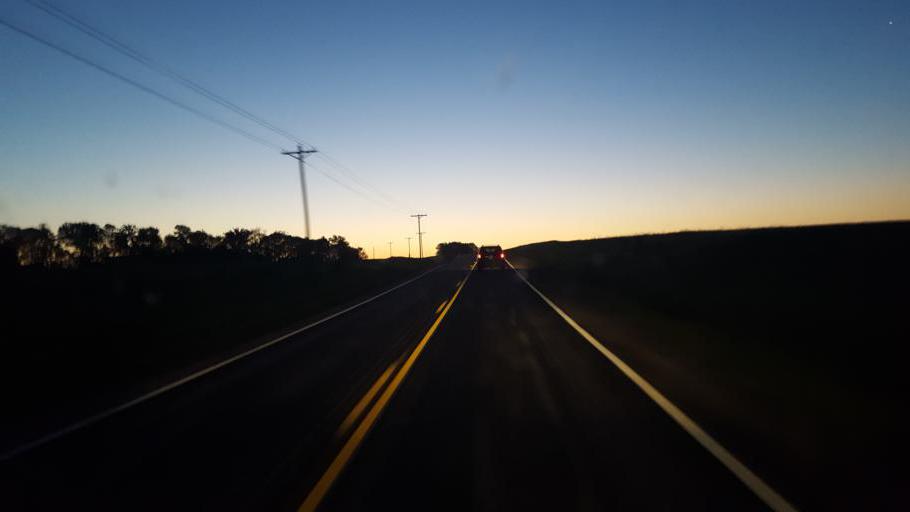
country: US
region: Missouri
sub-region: Mercer County
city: Princeton
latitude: 40.4168
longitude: -93.4949
